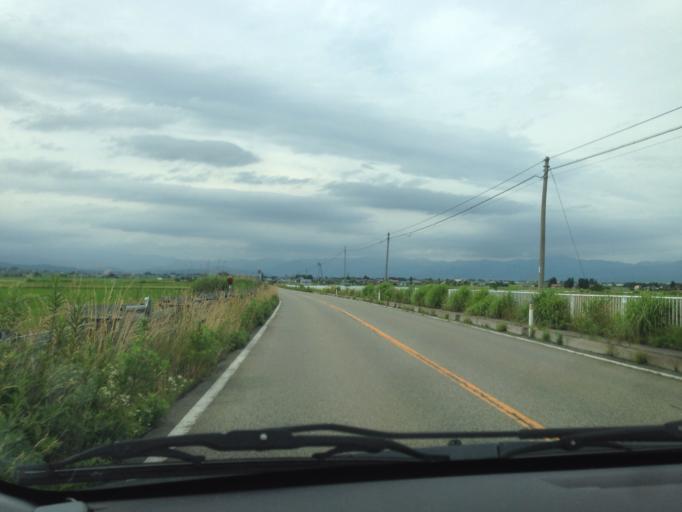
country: JP
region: Fukushima
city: Kitakata
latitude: 37.4747
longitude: 139.8394
